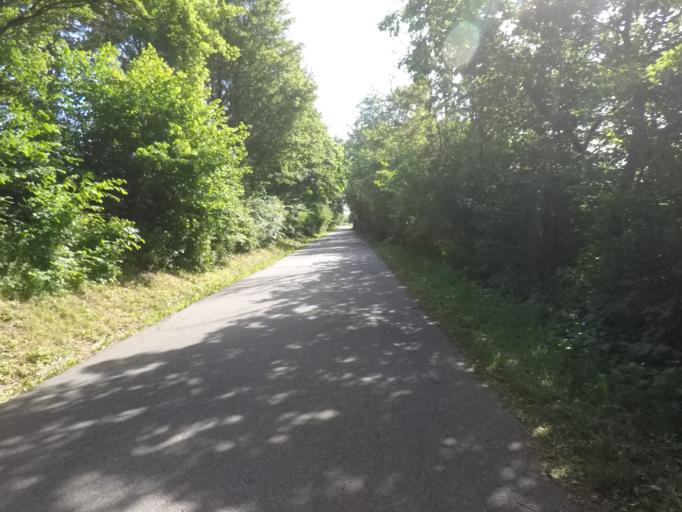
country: SE
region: Skane
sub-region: Malmo
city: Oxie
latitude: 55.5840
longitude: 13.1360
